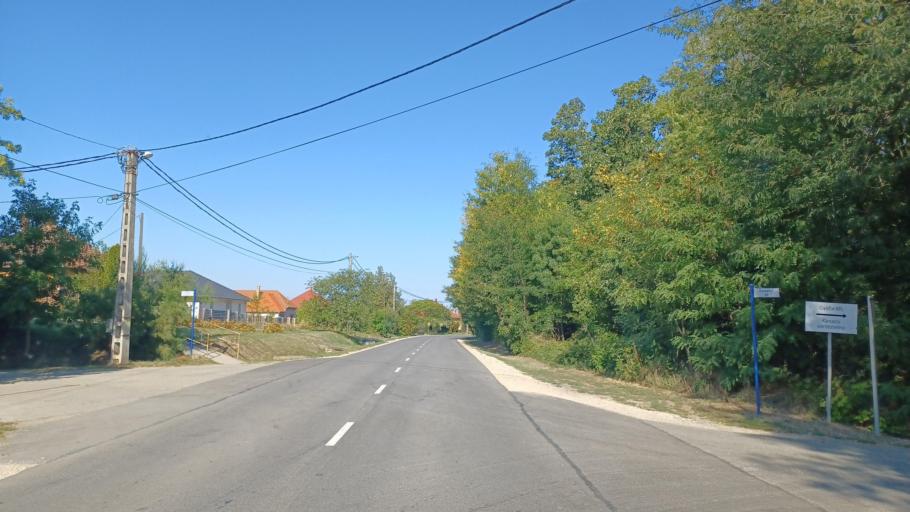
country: HU
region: Tolna
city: Nemetker
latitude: 46.6772
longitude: 18.8103
